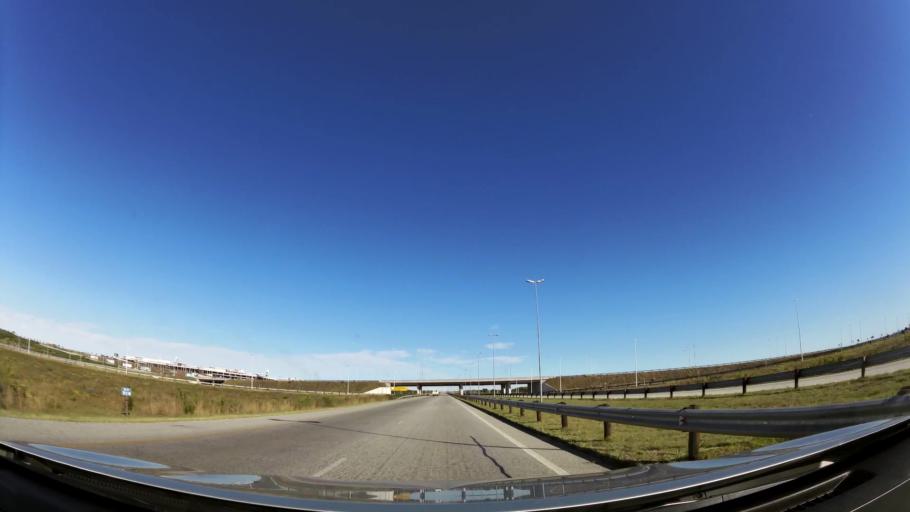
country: ZA
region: Eastern Cape
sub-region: Nelson Mandela Bay Metropolitan Municipality
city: Port Elizabeth
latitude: -33.9469
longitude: 25.4675
